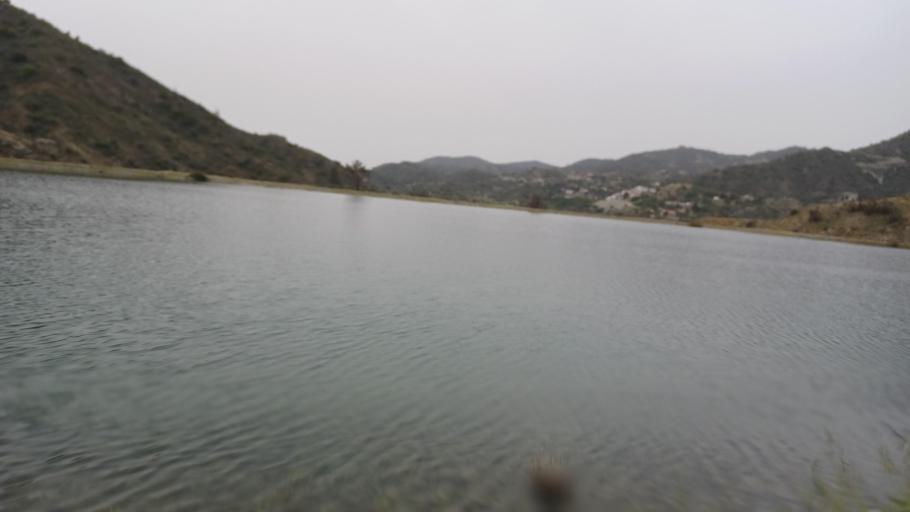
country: CY
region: Limassol
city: Parekklisha
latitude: 34.8398
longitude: 33.1219
